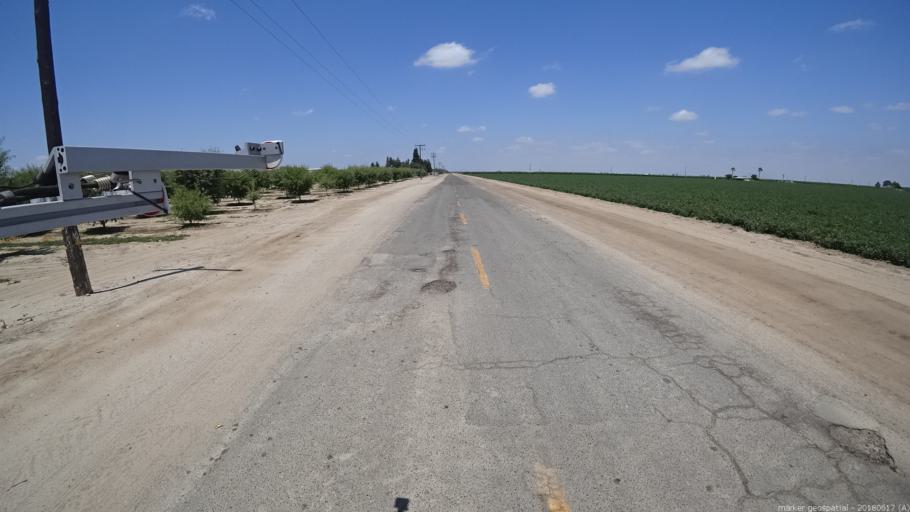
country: US
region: California
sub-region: Fresno County
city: Kerman
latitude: 36.8189
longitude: -120.1509
